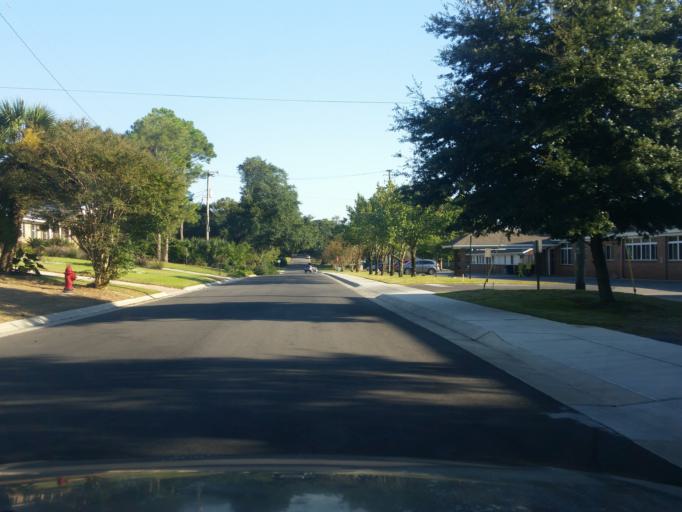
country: US
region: Florida
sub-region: Escambia County
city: Goulding
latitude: 30.4579
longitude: -87.1968
